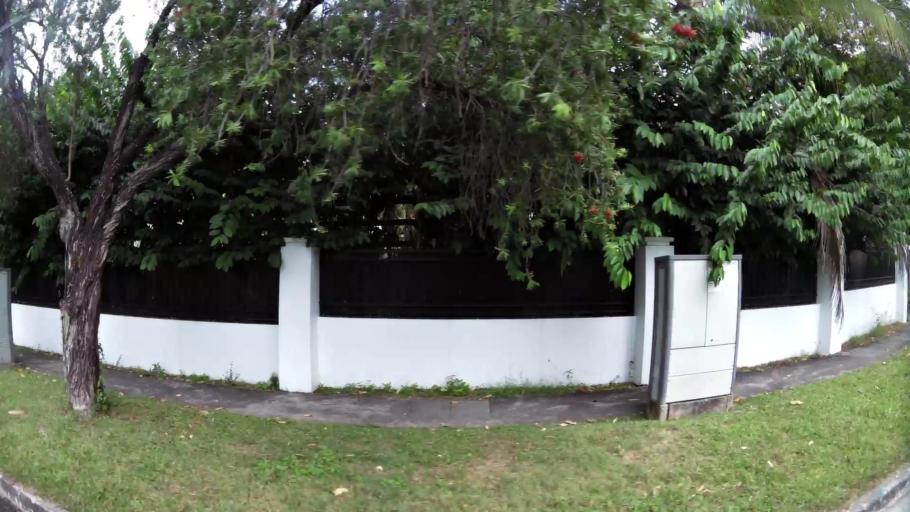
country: SG
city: Singapore
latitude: 1.3376
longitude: 103.7701
